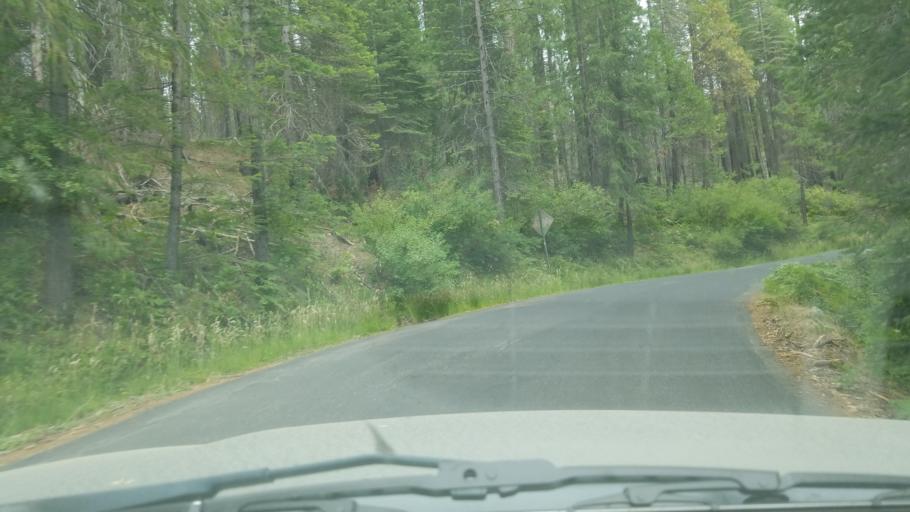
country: US
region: California
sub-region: Mariposa County
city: Yosemite Valley
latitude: 37.8560
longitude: -119.8644
